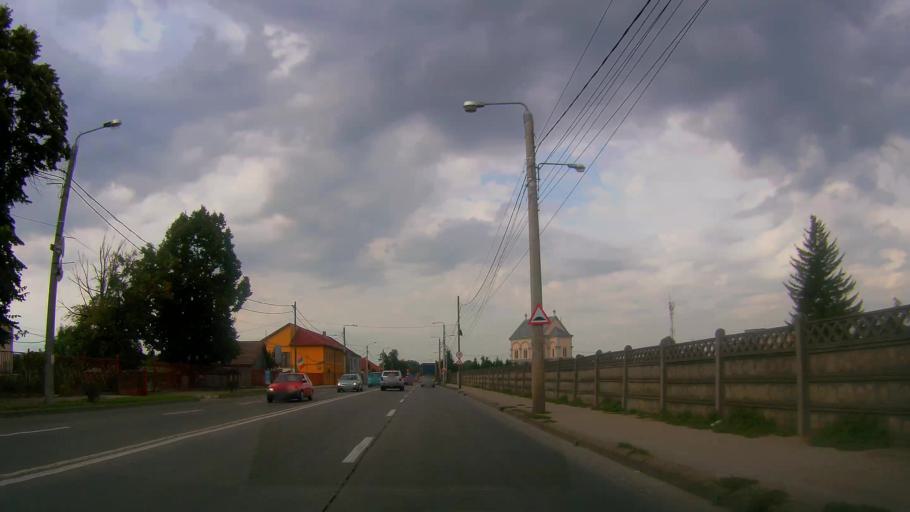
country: RO
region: Satu Mare
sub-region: Municipiul Satu Mare
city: Satu Mare
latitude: 47.7927
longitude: 22.8927
